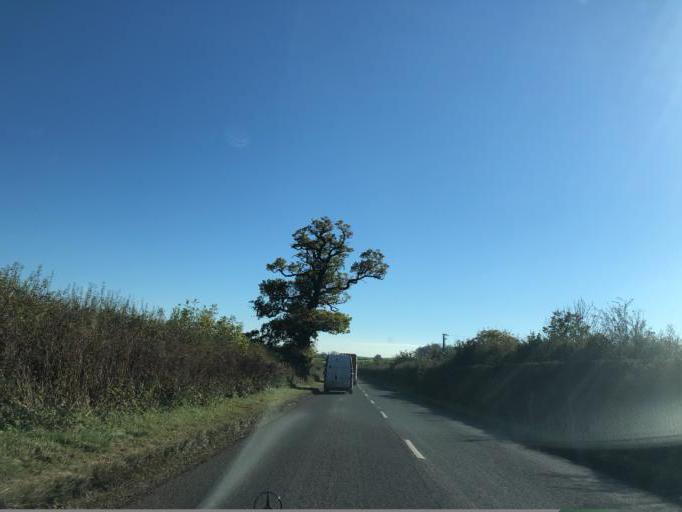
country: GB
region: England
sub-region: Warwickshire
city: Royal Leamington Spa
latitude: 52.2566
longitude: -1.5275
